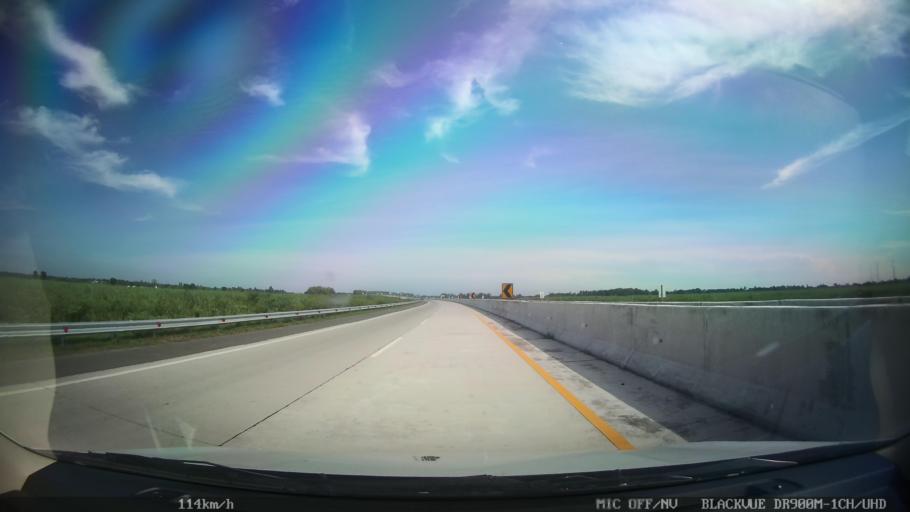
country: ID
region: North Sumatra
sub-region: Kabupaten Langkat
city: Stabat
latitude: 3.6949
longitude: 98.5405
